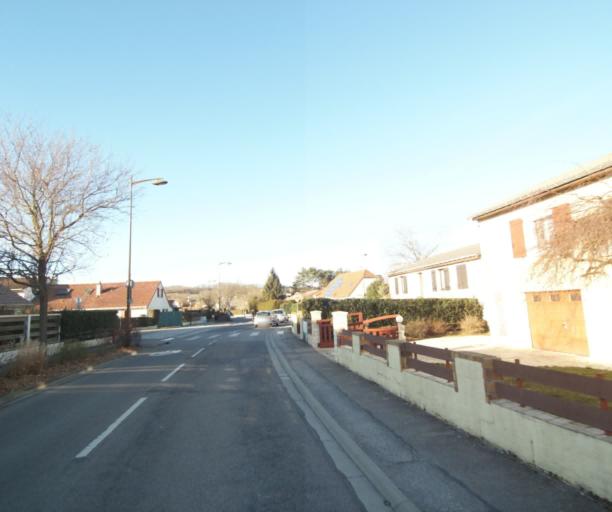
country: FR
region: Lorraine
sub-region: Departement de Meurthe-et-Moselle
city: Pulnoy
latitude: 48.7084
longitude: 6.2547
